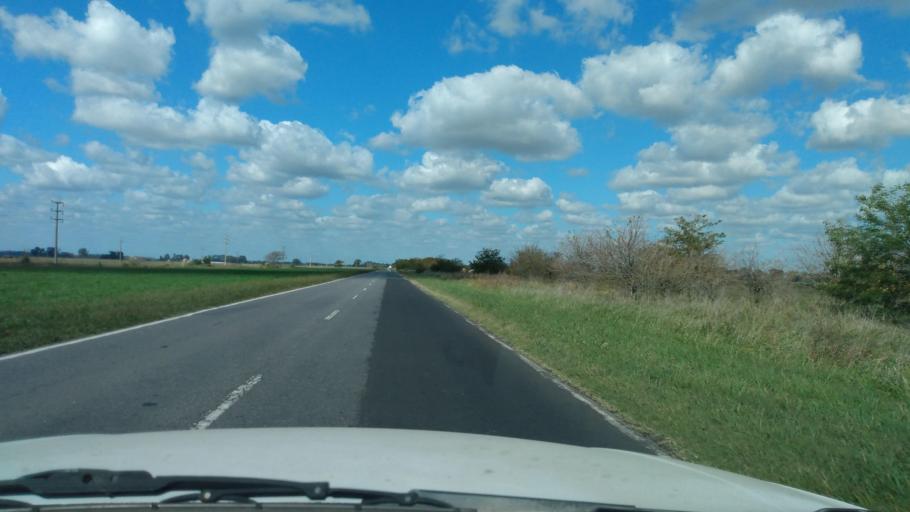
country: AR
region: Buenos Aires
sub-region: Partido de Navarro
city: Navarro
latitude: -34.9060
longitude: -59.3324
